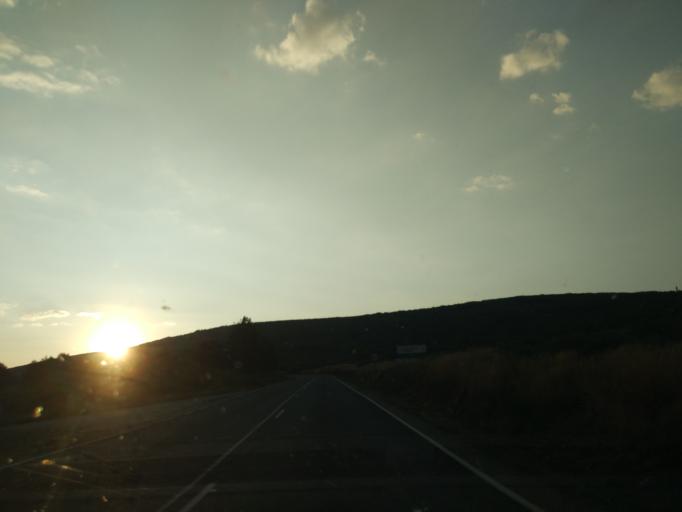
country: ES
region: Castille and Leon
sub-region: Provincia de Avila
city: San Martin del Pimpollar
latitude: 40.3729
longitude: -5.0205
